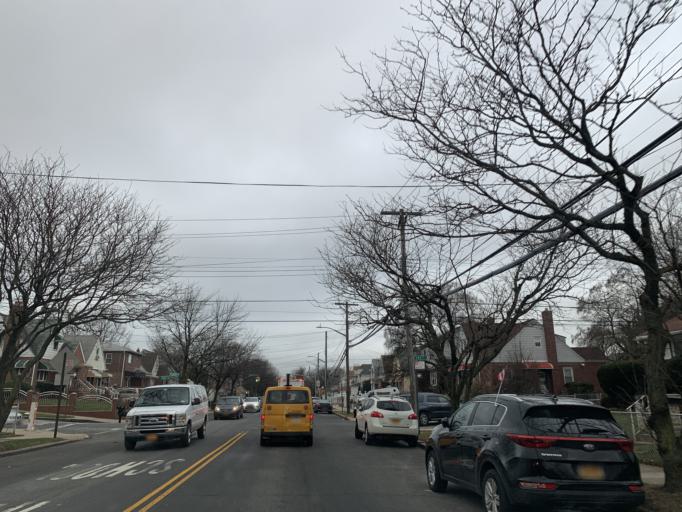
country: US
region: New York
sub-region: Queens County
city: Jamaica
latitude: 40.6840
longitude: -73.8022
